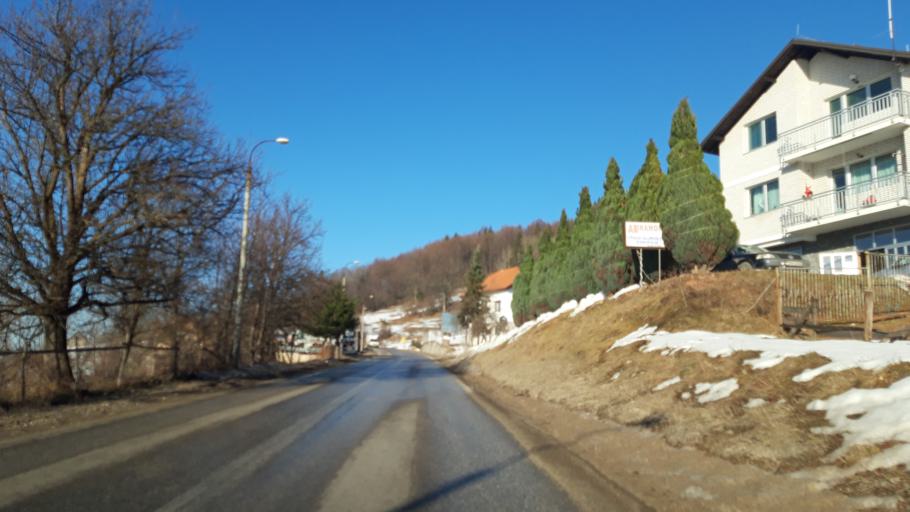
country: BA
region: Republika Srpska
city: Pale
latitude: 43.8949
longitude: 18.6362
